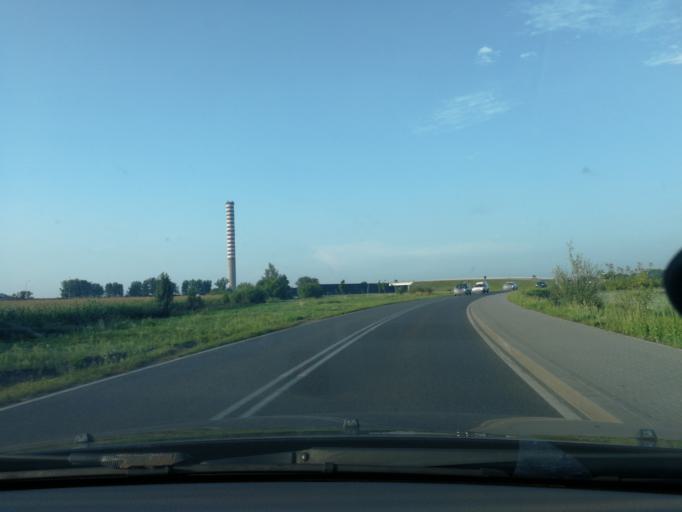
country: PL
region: Masovian Voivodeship
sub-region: Powiat pruszkowski
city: Brwinow
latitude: 52.1632
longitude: 20.7367
